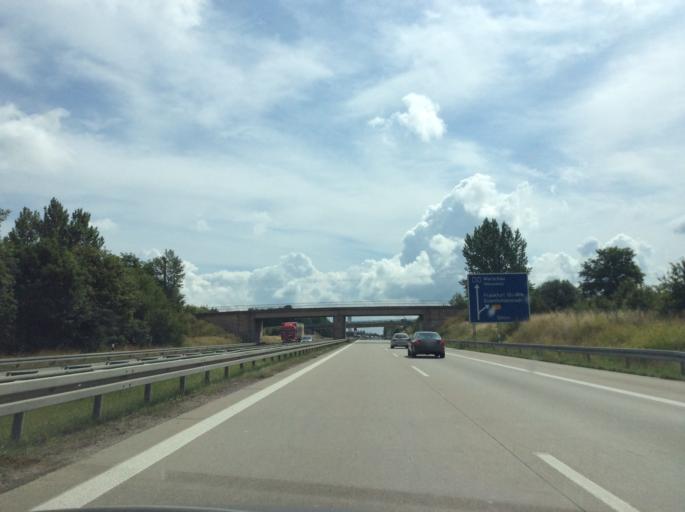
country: DE
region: Brandenburg
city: Frankfurt (Oder)
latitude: 52.3201
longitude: 14.5001
